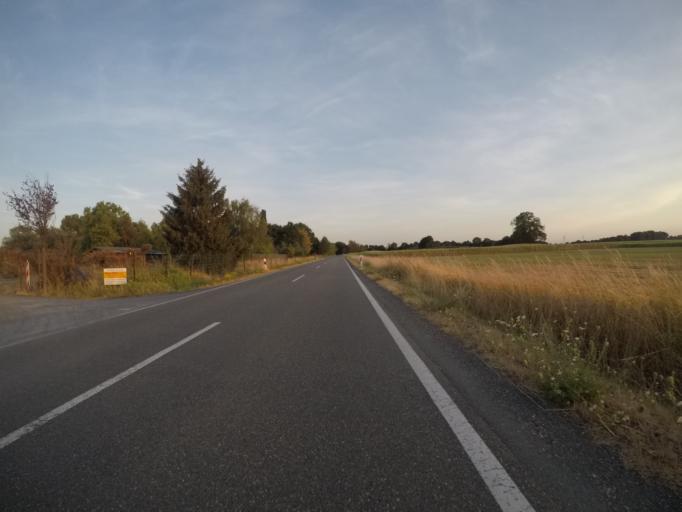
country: DE
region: North Rhine-Westphalia
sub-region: Regierungsbezirk Dusseldorf
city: Bocholt
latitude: 51.8532
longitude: 6.5487
